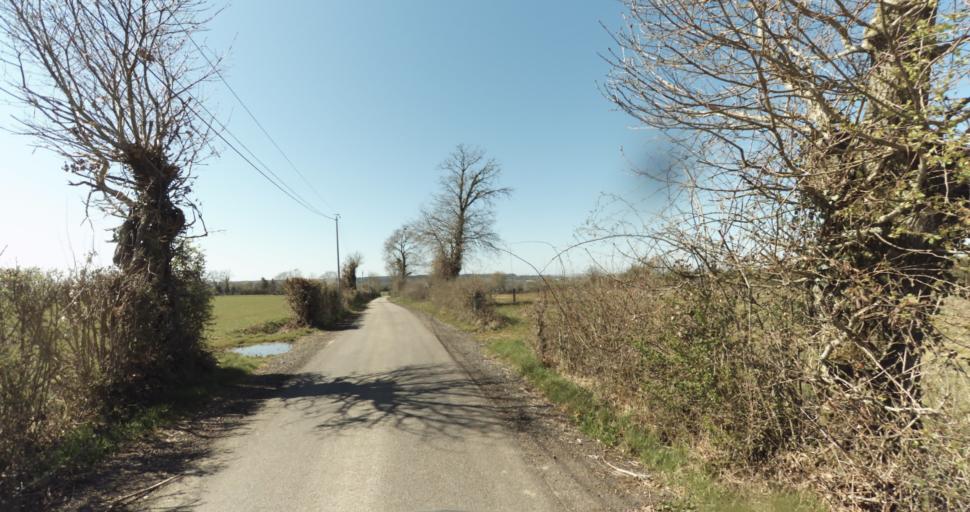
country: FR
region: Lower Normandy
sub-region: Departement du Calvados
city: Livarot
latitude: 49.0143
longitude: 0.1072
